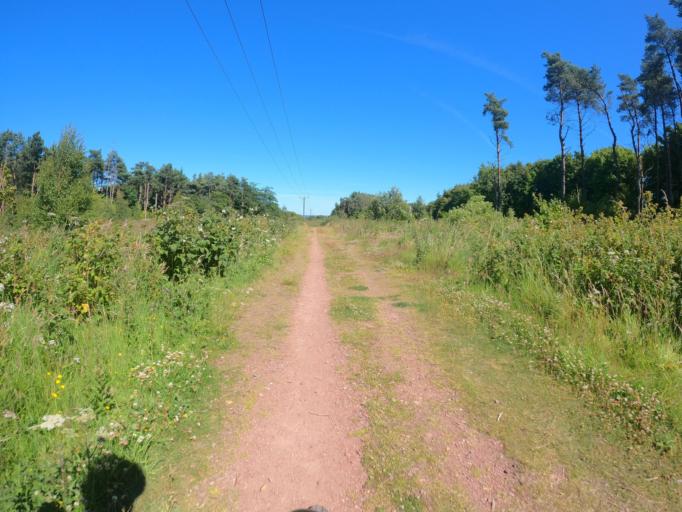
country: GB
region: Scotland
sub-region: West Lothian
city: Livingston
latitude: 55.9180
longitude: -3.5427
